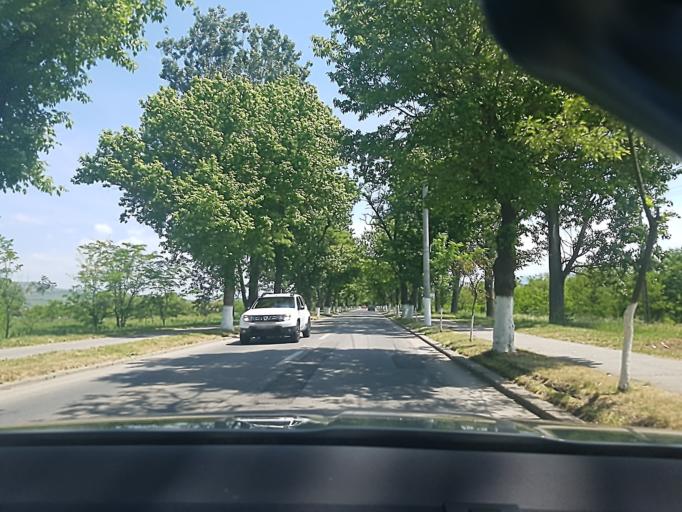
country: RO
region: Hunedoara
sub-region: Comuna Calan
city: Calan
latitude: 45.7351
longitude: 23.0051
